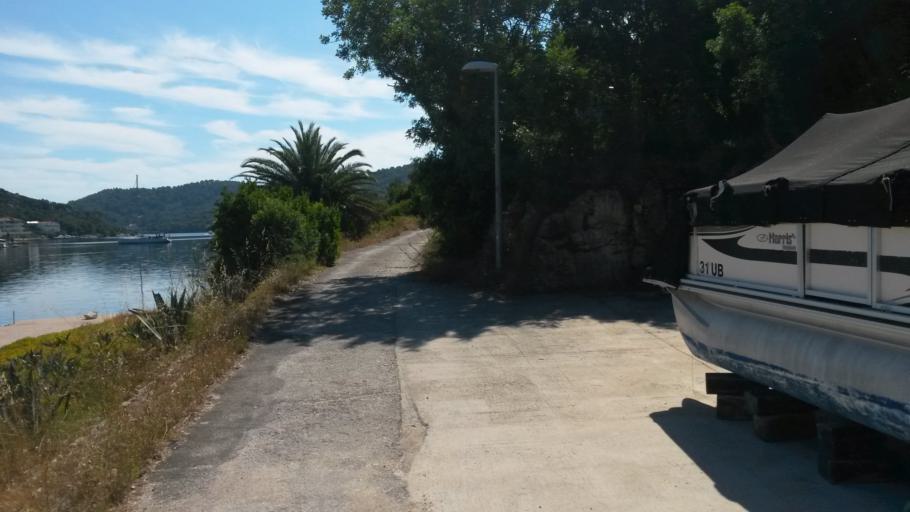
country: HR
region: Dubrovacko-Neretvanska
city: Smokvica
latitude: 42.7670
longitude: 16.8236
